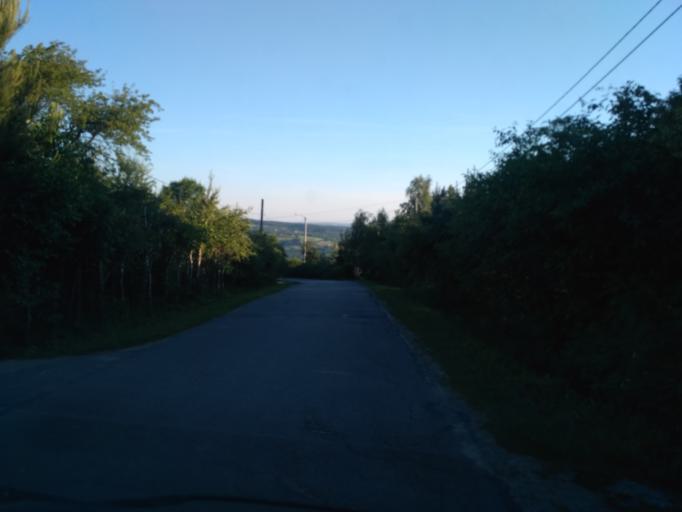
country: PL
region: Subcarpathian Voivodeship
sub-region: Powiat rzeszowski
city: Lubenia
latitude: 49.9210
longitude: 21.9133
